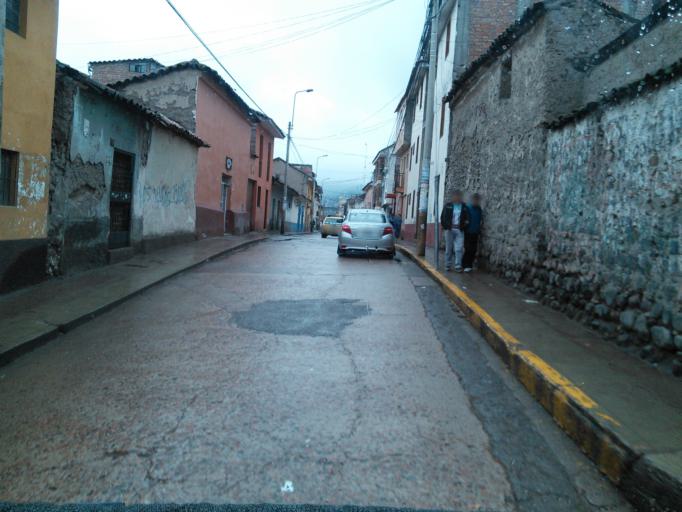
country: PE
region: Ayacucho
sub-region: Provincia de Huamanga
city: Ayacucho
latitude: -13.1580
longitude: -74.2283
